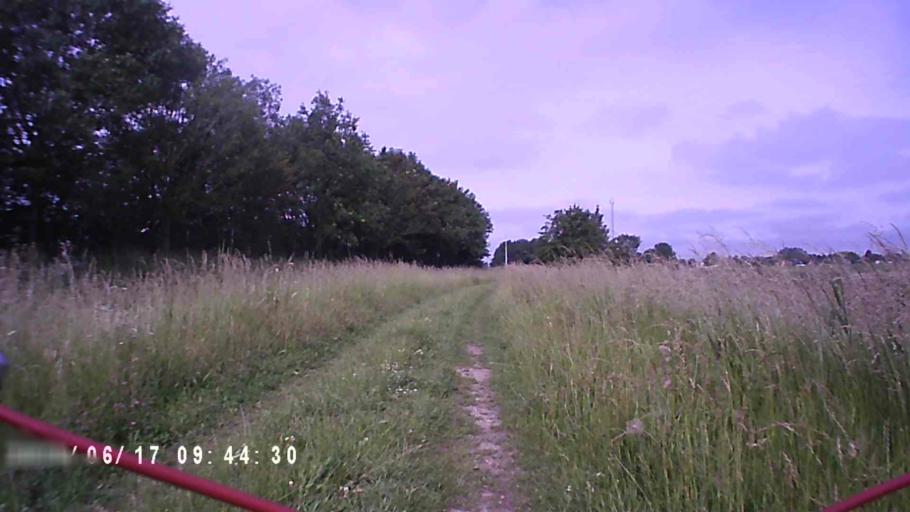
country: NL
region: Groningen
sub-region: Gemeente De Marne
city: Ulrum
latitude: 53.3523
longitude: 6.3436
